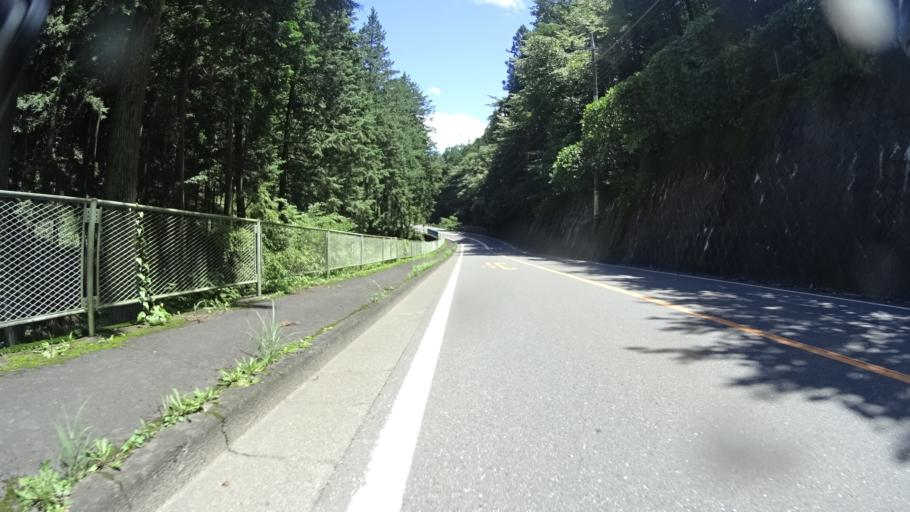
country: JP
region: Tokyo
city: Ome
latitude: 35.8275
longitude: 139.2170
